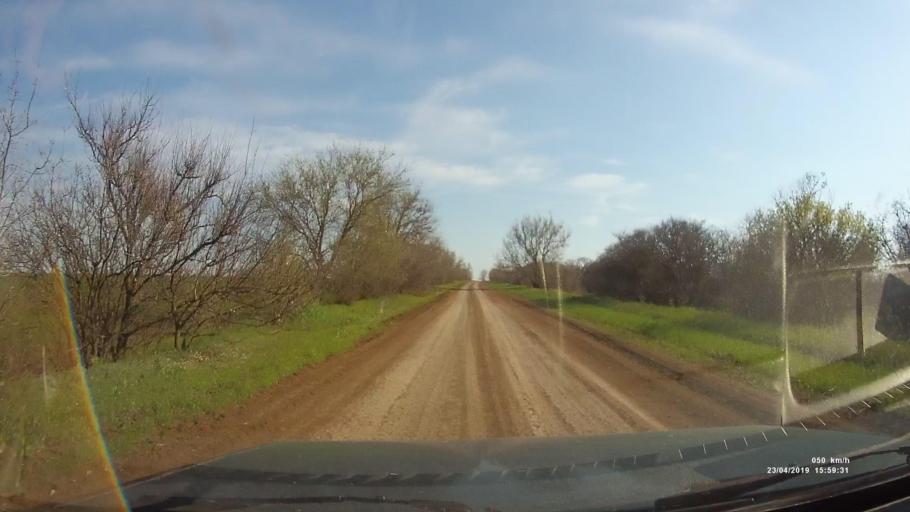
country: RU
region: Rostov
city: Remontnoye
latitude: 46.5162
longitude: 43.1096
